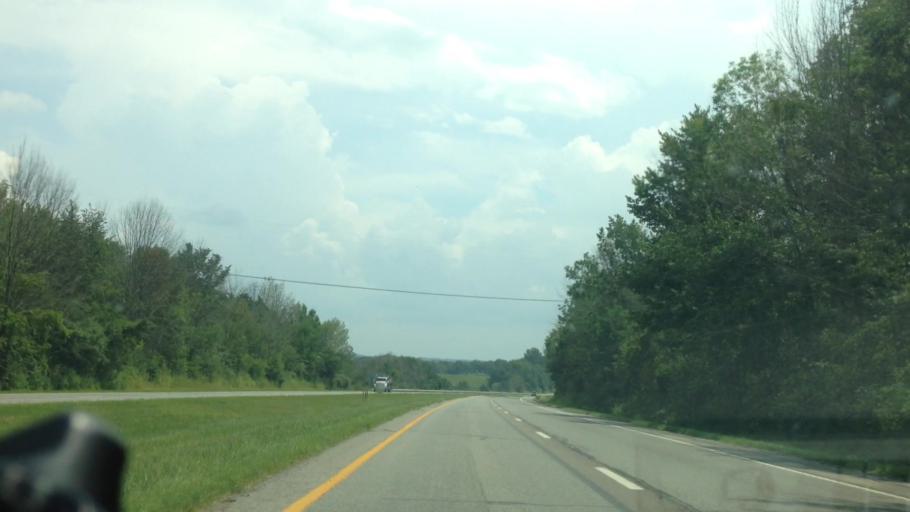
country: US
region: Ohio
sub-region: Stark County
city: Canal Fulton
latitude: 40.8680
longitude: -81.5894
